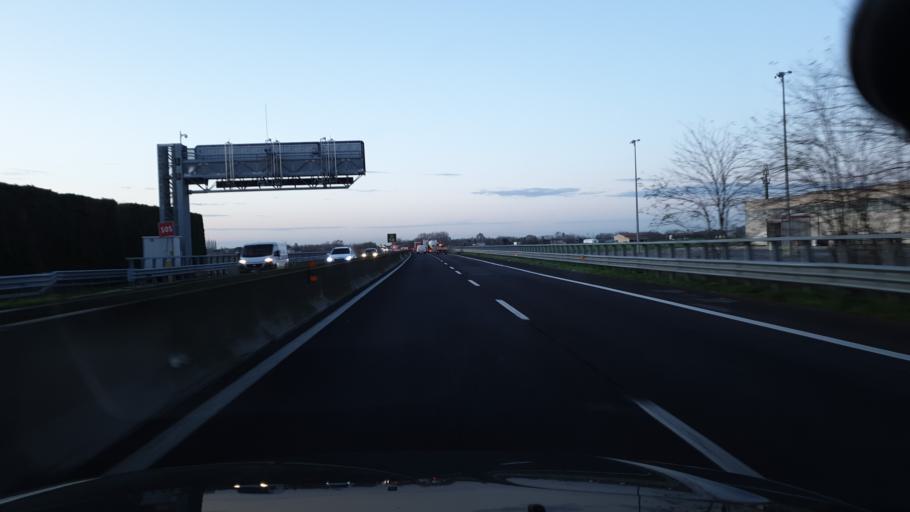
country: IT
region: Veneto
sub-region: Provincia di Rovigo
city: Villamarzana
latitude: 45.0154
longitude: 11.6874
